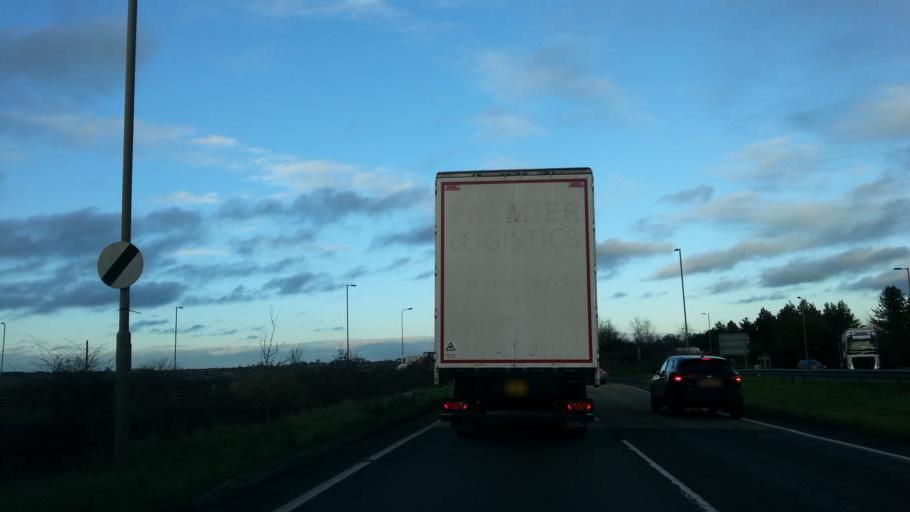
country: GB
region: England
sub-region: Northamptonshire
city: Brackley
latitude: 52.0116
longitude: -1.1581
